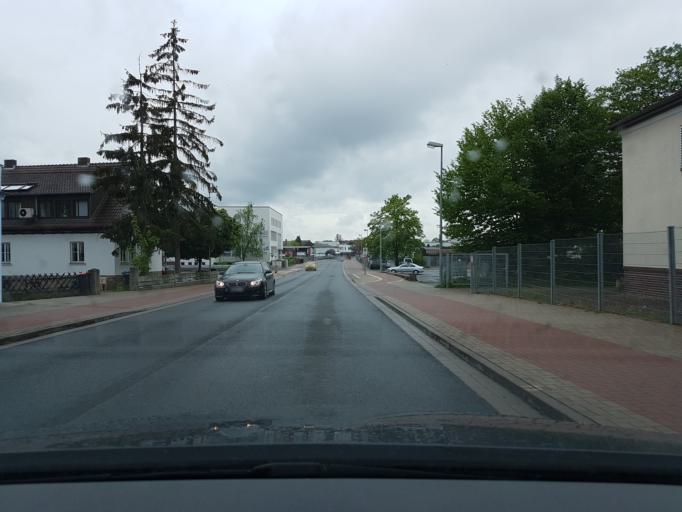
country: DE
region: Lower Saxony
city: Hameln
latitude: 52.0939
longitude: 9.3737
